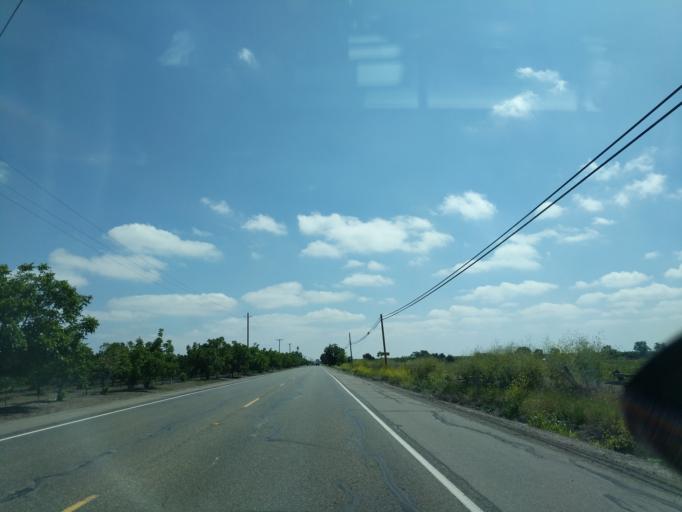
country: US
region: California
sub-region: San Joaquin County
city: Garden Acres
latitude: 37.9481
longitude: -121.2059
